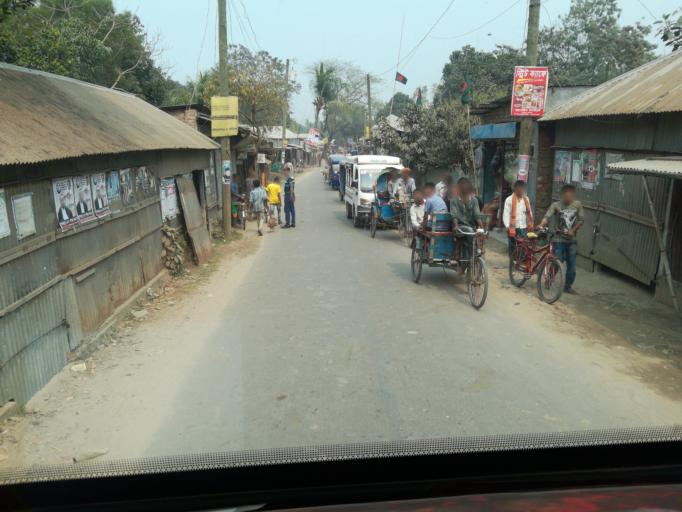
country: BD
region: Dhaka
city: Nagarpur
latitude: 23.9021
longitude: 89.8751
